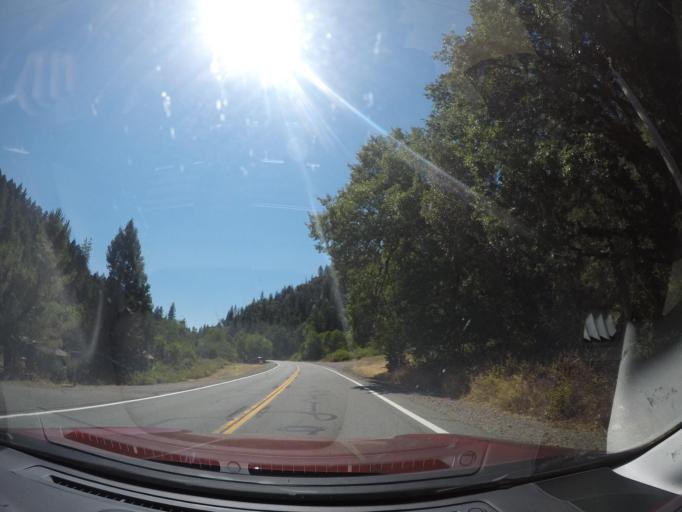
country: US
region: California
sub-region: Shasta County
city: Bella Vista
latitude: 40.7517
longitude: -122.0442
